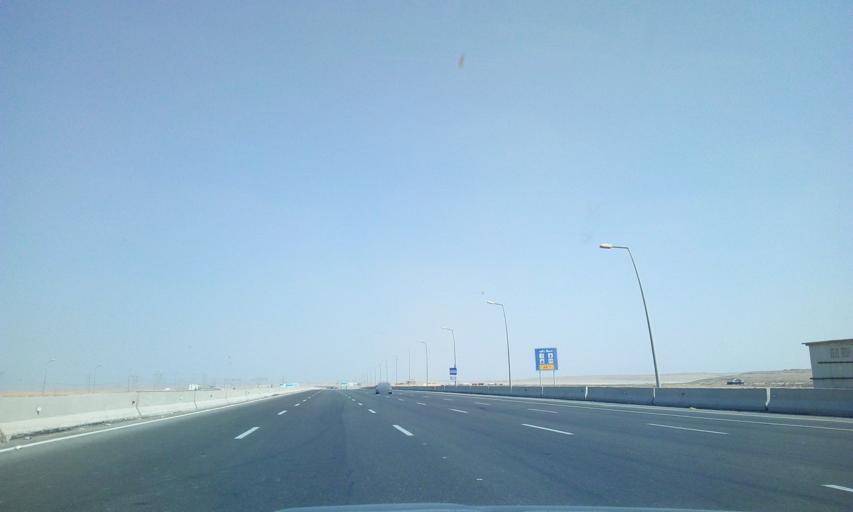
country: EG
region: As Suways
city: Ain Sukhna
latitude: 29.7797
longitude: 31.9106
